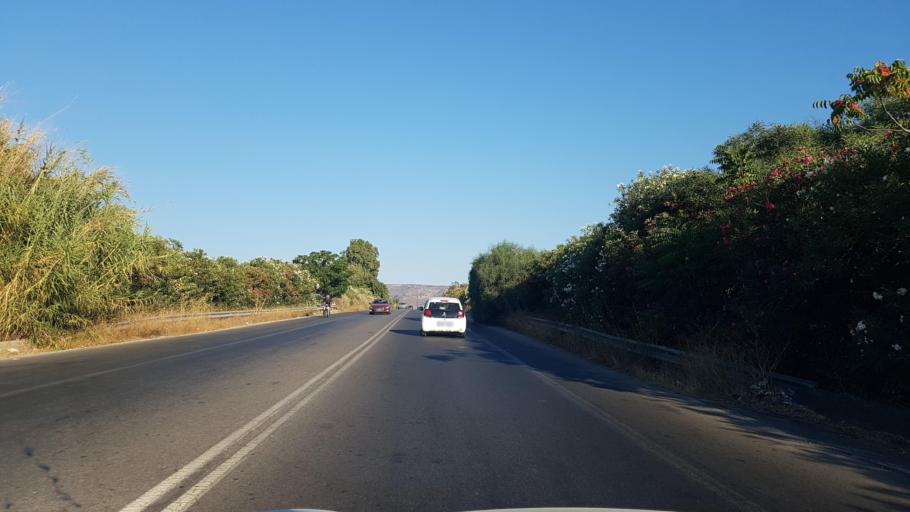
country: GR
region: Crete
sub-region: Nomos Chanias
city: Daratsos
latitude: 35.5029
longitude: 23.9839
